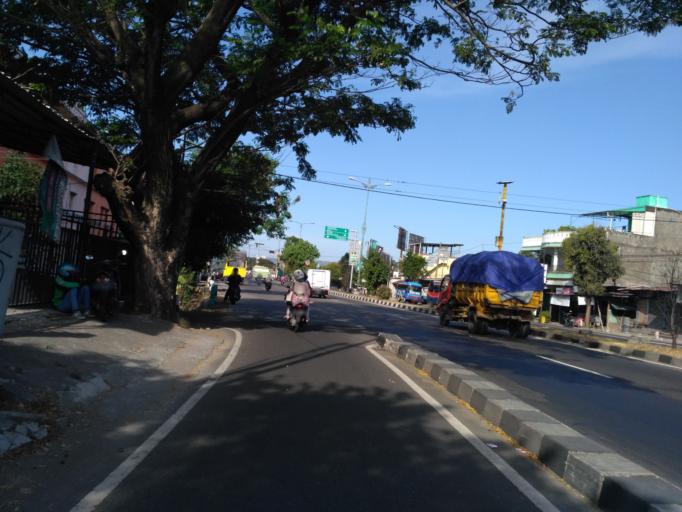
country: ID
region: Daerah Istimewa Yogyakarta
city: Sewon
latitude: -7.8363
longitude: 110.3905
